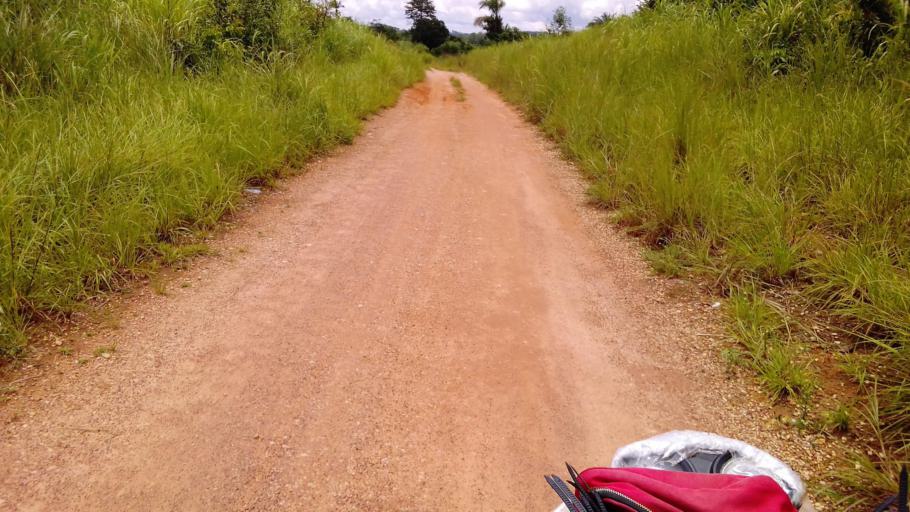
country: SL
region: Eastern Province
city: Koidu
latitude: 8.6725
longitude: -10.9553
